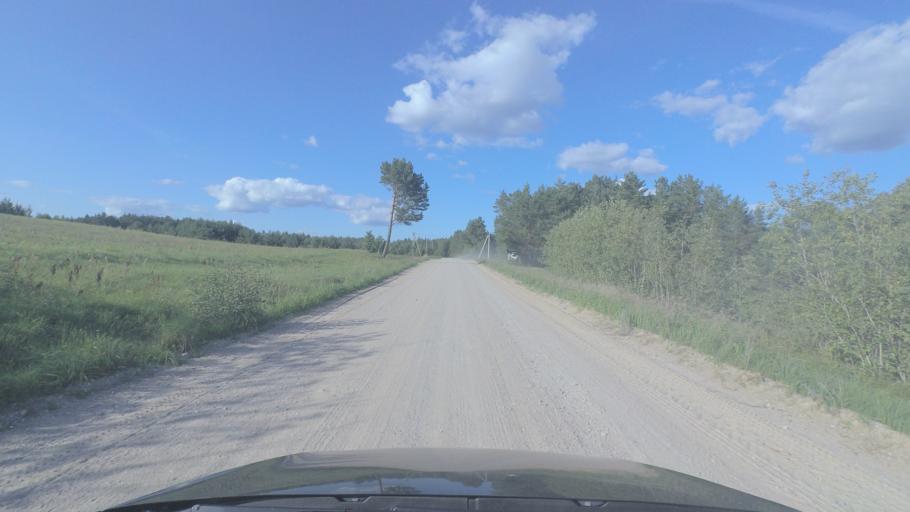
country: LT
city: Pabrade
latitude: 55.1390
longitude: 25.7112
